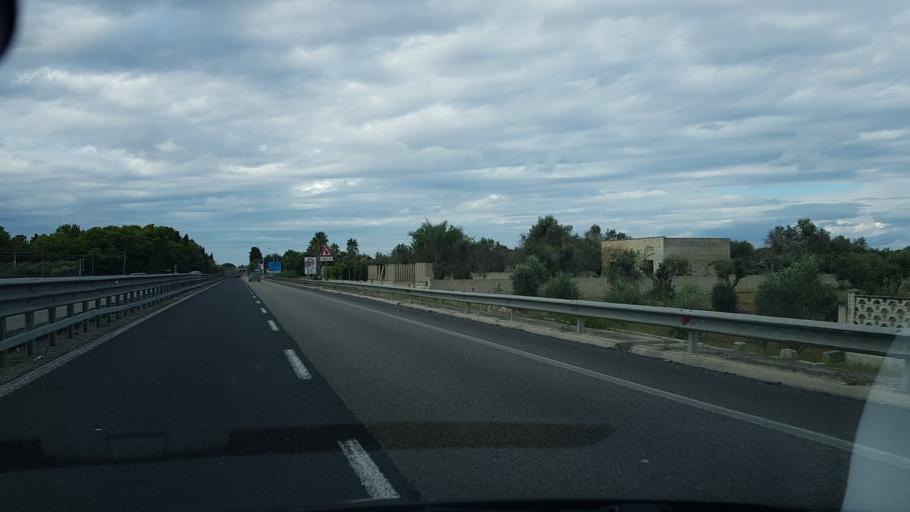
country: IT
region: Apulia
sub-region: Provincia di Lecce
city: Cavallino
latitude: 40.3017
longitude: 18.1930
